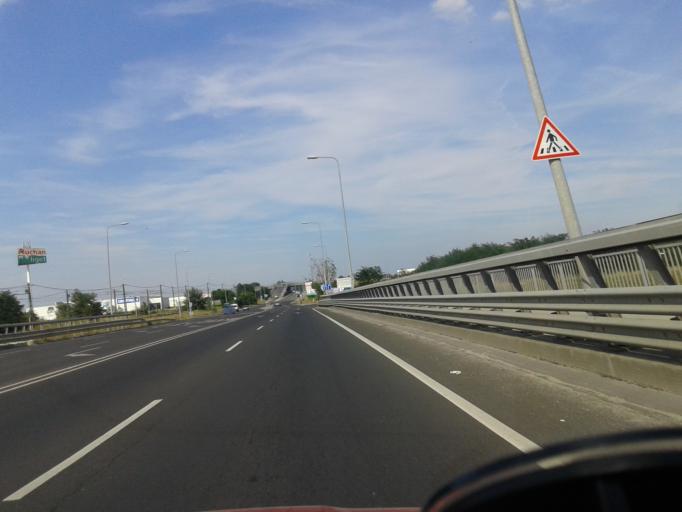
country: HU
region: Pest
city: Csomor
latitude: 47.5354
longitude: 19.2437
